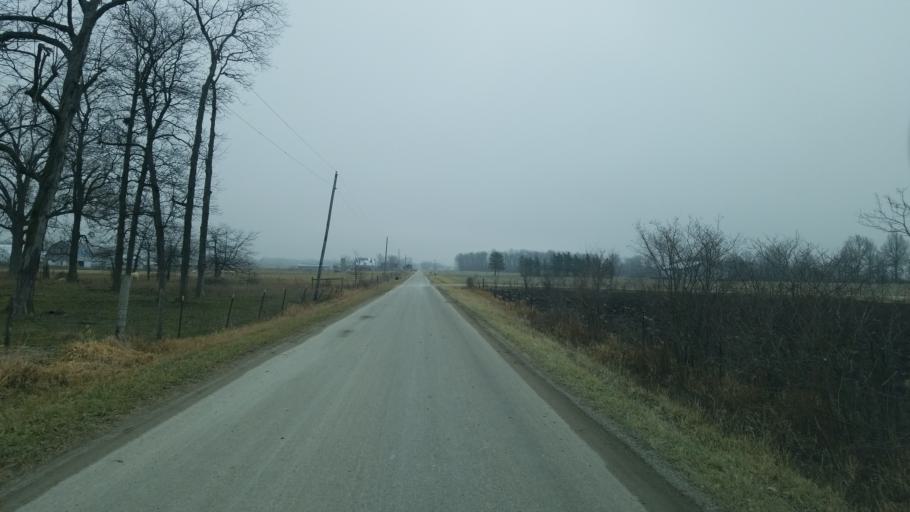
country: US
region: Indiana
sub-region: Adams County
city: Geneva
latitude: 40.5711
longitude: -84.8982
